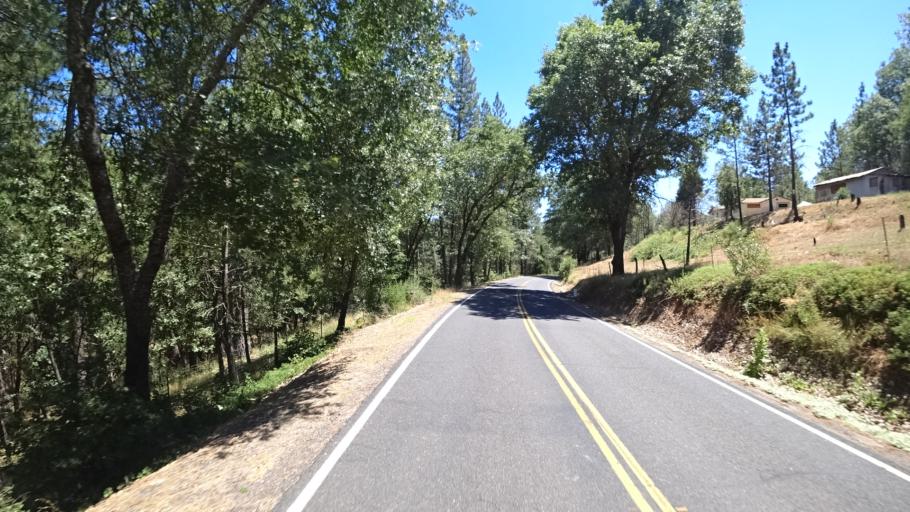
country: US
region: California
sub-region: Calaveras County
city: Mountain Ranch
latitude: 38.3055
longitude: -120.5065
